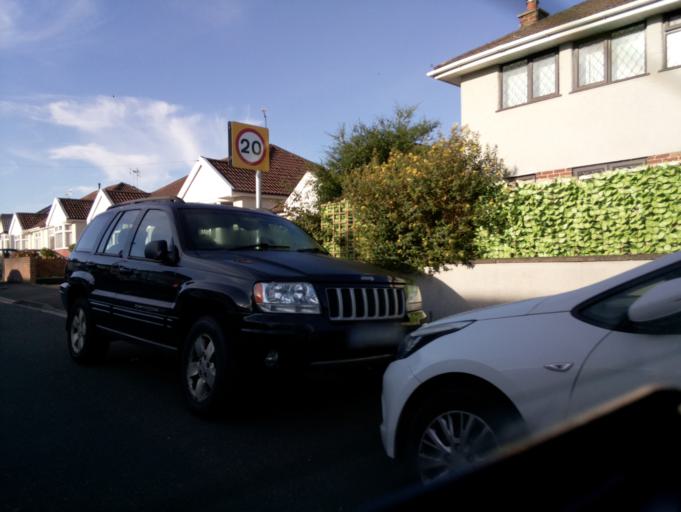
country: GB
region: England
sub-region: South Gloucestershire
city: Mangotsfield
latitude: 51.4865
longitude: -2.5009
